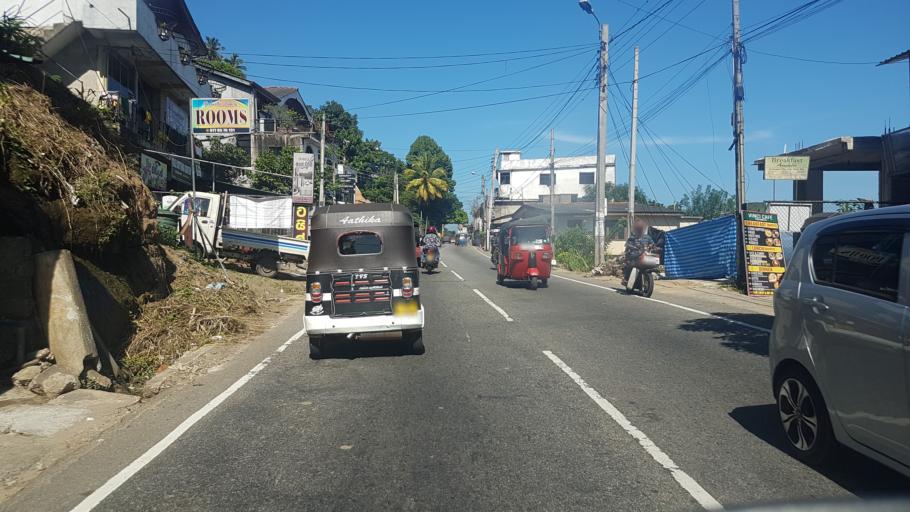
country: LK
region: Central
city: Kandy
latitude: 7.2878
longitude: 80.6579
